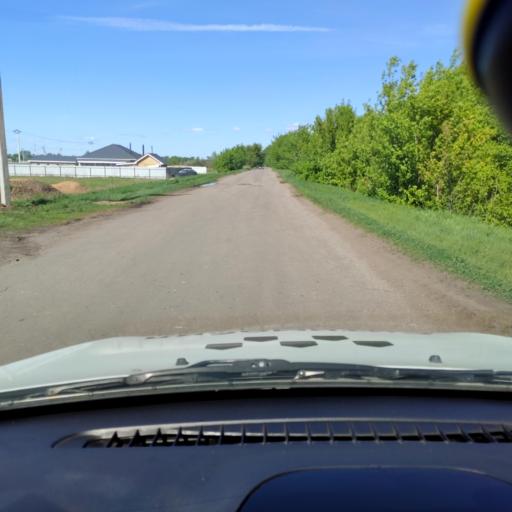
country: RU
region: Samara
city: Tol'yatti
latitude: 53.6659
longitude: 49.4344
